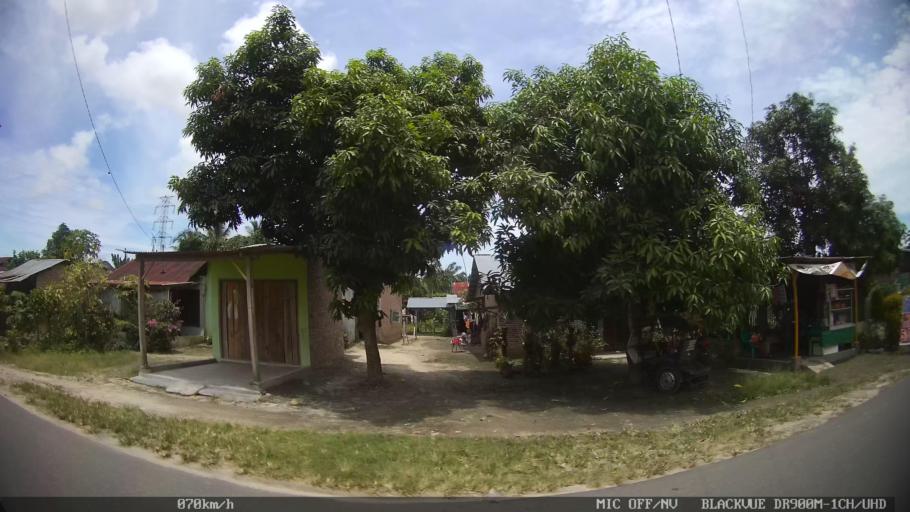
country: ID
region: North Sumatra
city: Percut
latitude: 3.5845
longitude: 98.8833
